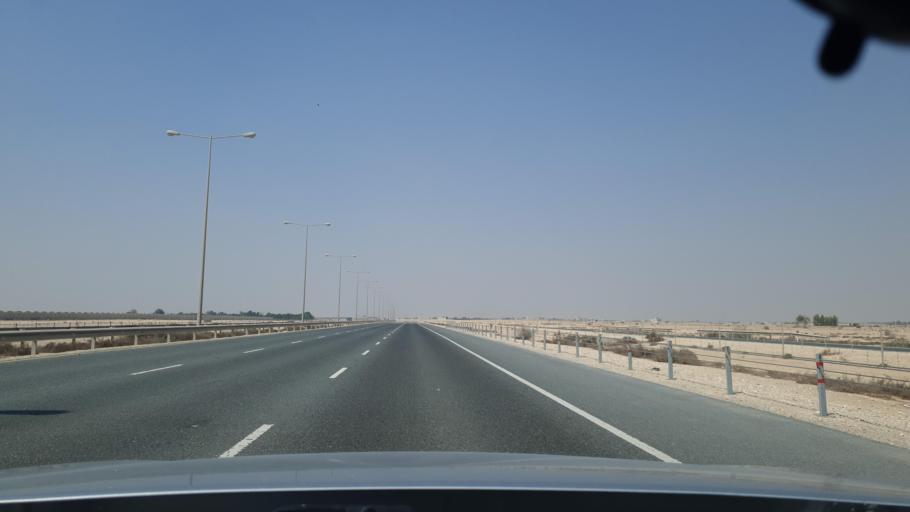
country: QA
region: Al Khawr
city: Al Khawr
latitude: 25.7696
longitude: 51.4153
